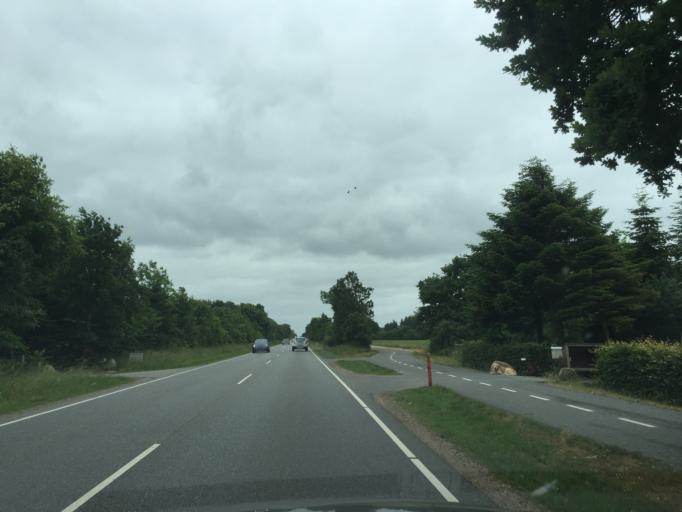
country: DK
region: South Denmark
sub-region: Esbjerg Kommune
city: Ribe
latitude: 55.3060
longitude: 8.7460
